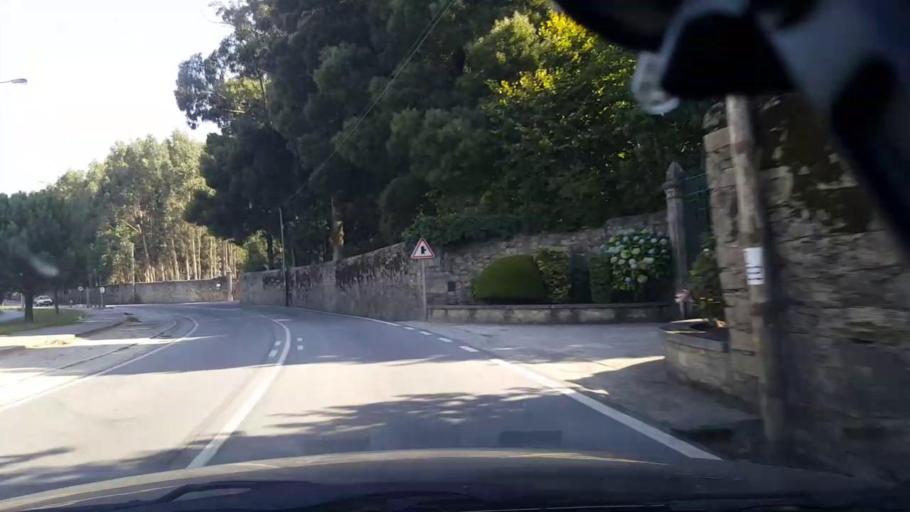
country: PT
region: Porto
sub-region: Vila do Conde
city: Arvore
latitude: 41.3650
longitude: -8.6704
